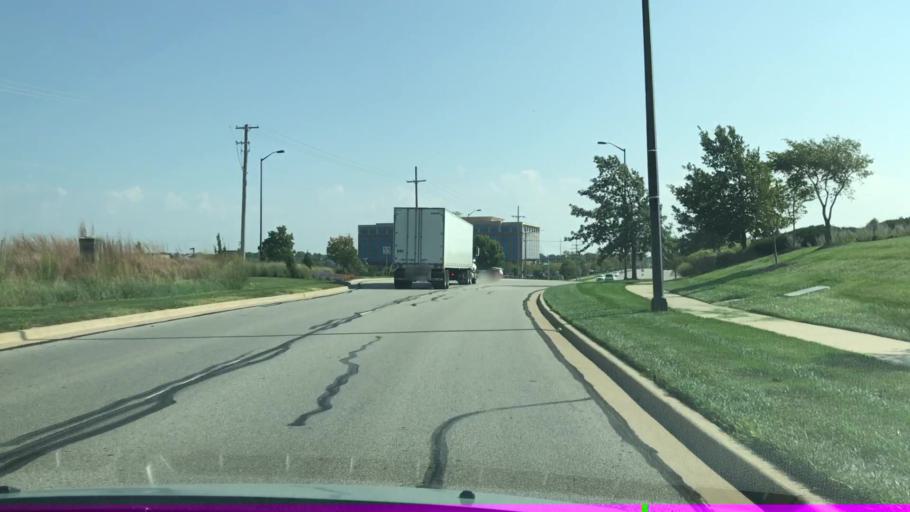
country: US
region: Kansas
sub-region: Johnson County
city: Lenexa
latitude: 38.9561
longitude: -94.7822
